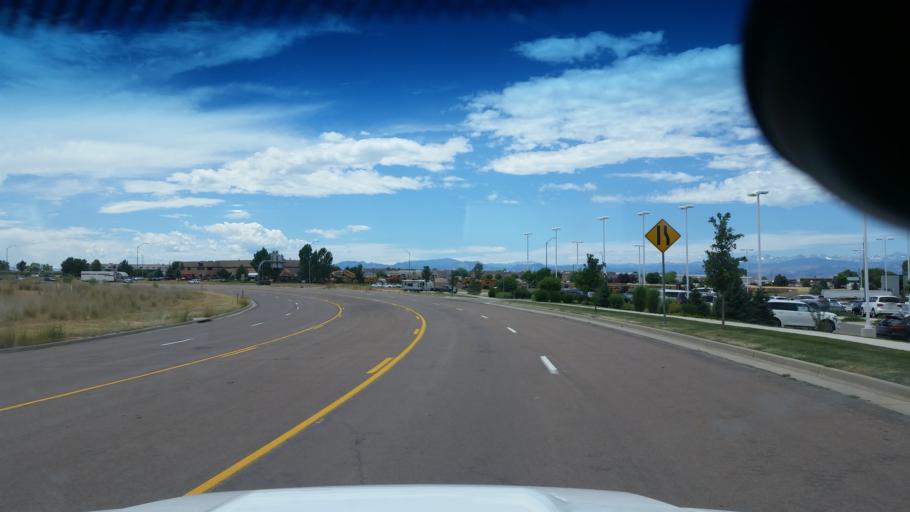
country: US
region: Colorado
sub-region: Weld County
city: Dacono
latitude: 40.0842
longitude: -104.9783
